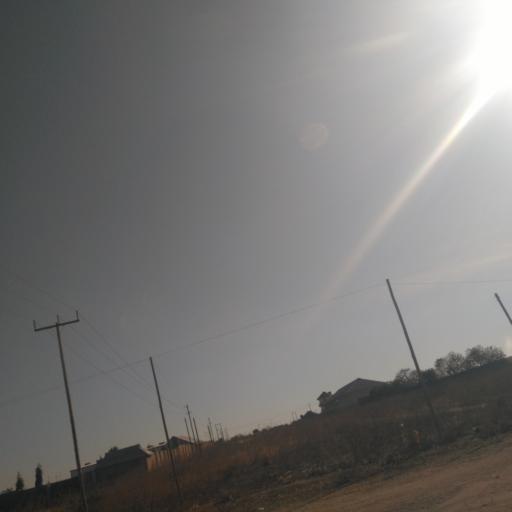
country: TZ
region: Dodoma
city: Dodoma
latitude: -6.1560
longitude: 35.7101
